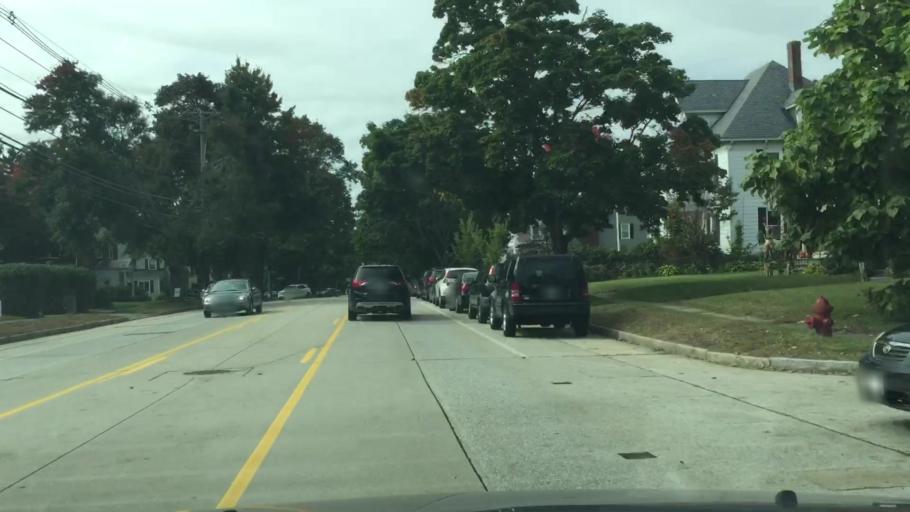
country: US
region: Massachusetts
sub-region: Middlesex County
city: Dracut
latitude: 42.6445
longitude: -71.2826
